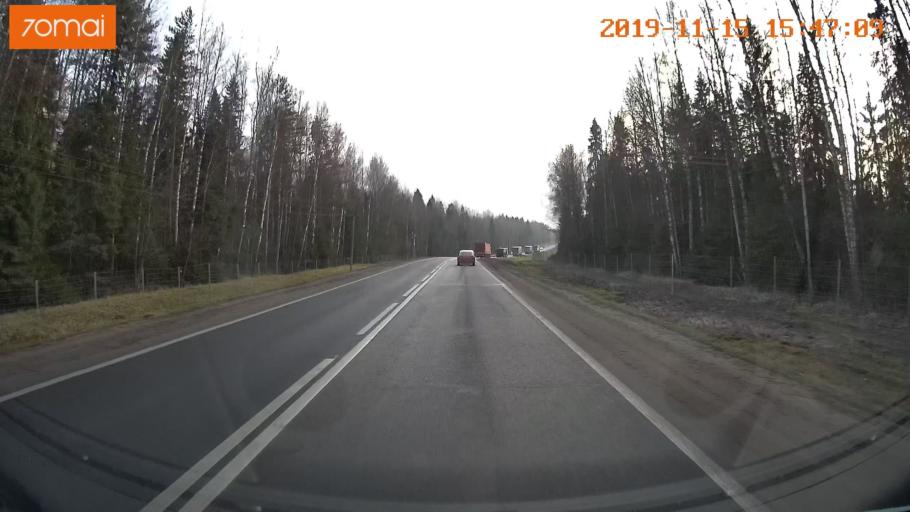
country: RU
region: Jaroslavl
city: Danilov
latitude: 57.9416
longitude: 40.0117
